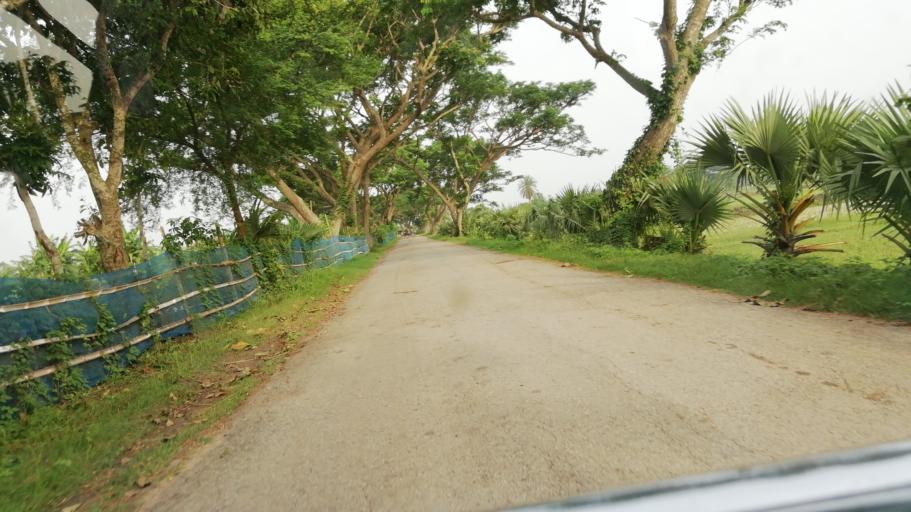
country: BD
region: Khulna
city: Bhatpara Abhaynagar
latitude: 23.0402
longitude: 89.3179
